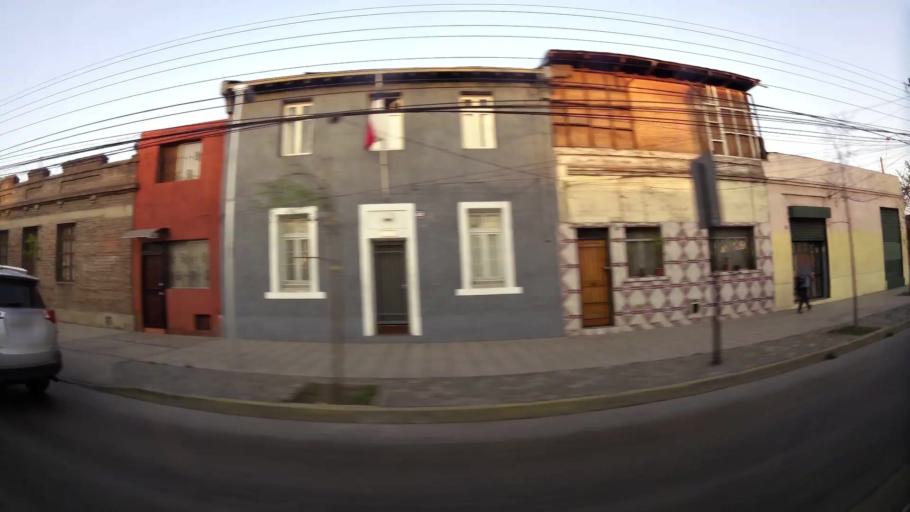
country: CL
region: Santiago Metropolitan
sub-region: Provincia de Santiago
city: Santiago
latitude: -33.4680
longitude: -70.6716
